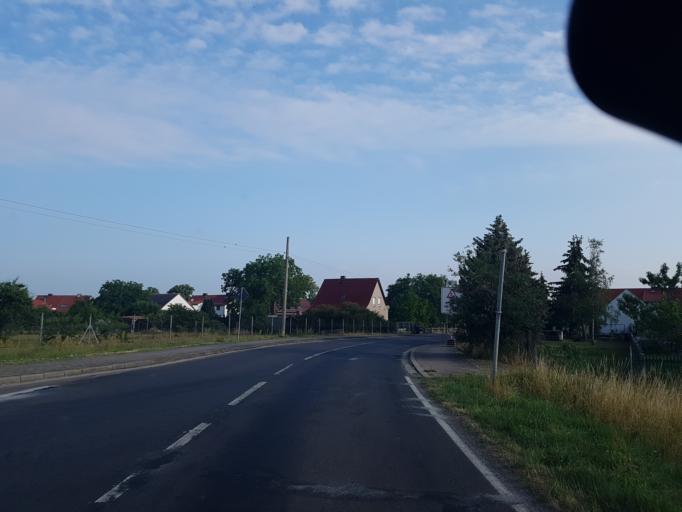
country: DE
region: Brandenburg
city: Schlieben
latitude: 51.7207
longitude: 13.3798
